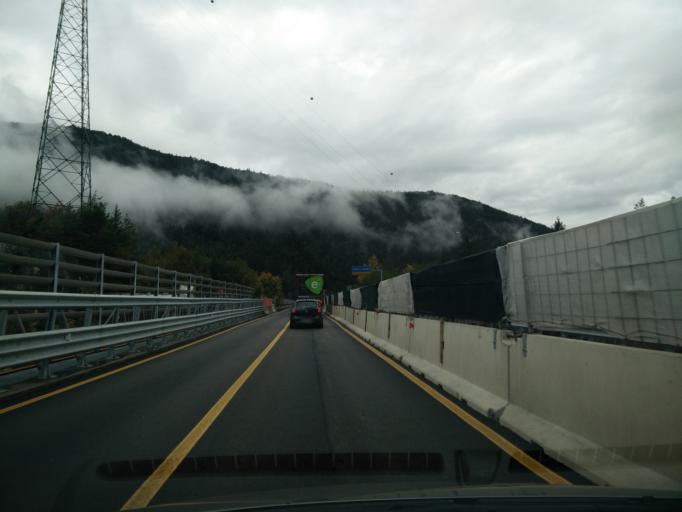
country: IT
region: Veneto
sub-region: Provincia di Belluno
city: Perarolo di Cadore
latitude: 46.4036
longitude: 12.3715
